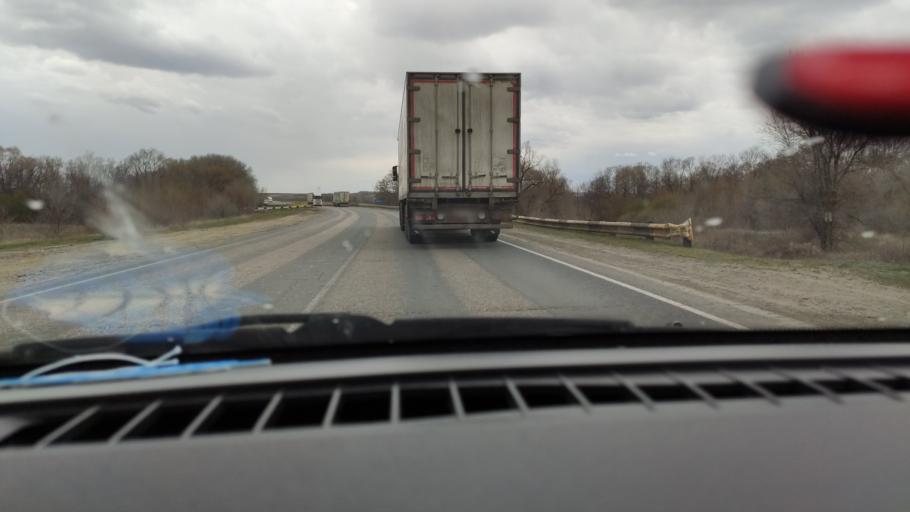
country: RU
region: Saratov
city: Sinodskoye
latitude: 51.9740
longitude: 46.6458
